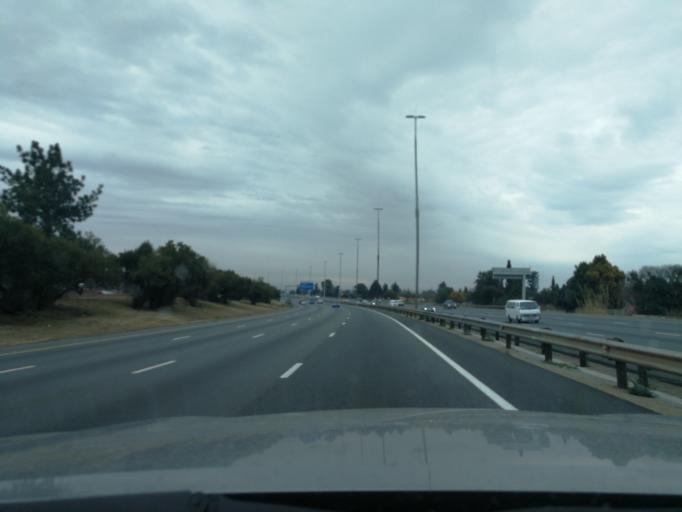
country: ZA
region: Gauteng
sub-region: Ekurhuleni Metropolitan Municipality
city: Germiston
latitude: -26.2742
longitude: 28.1492
